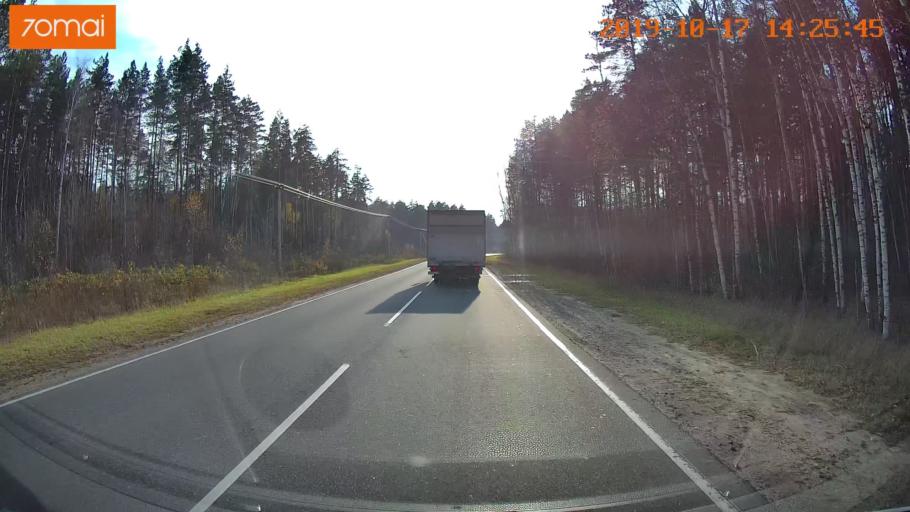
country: RU
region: Moskovskaya
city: Radovitskiy
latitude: 54.9976
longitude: 39.9753
